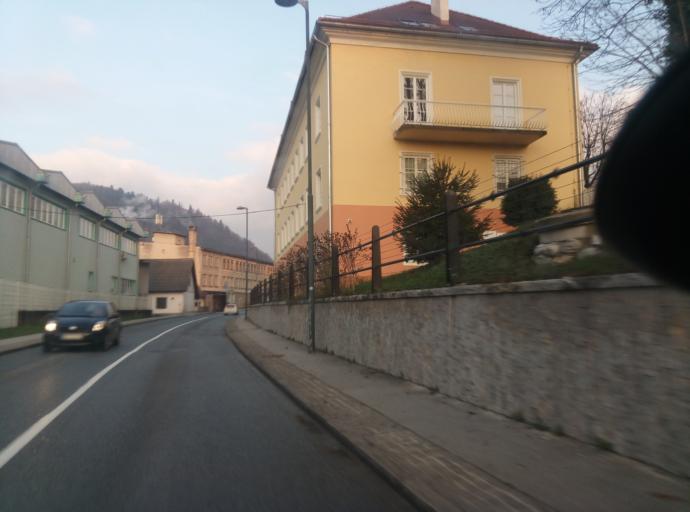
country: SI
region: Kranj
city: Kranj
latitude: 46.2359
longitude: 14.3550
